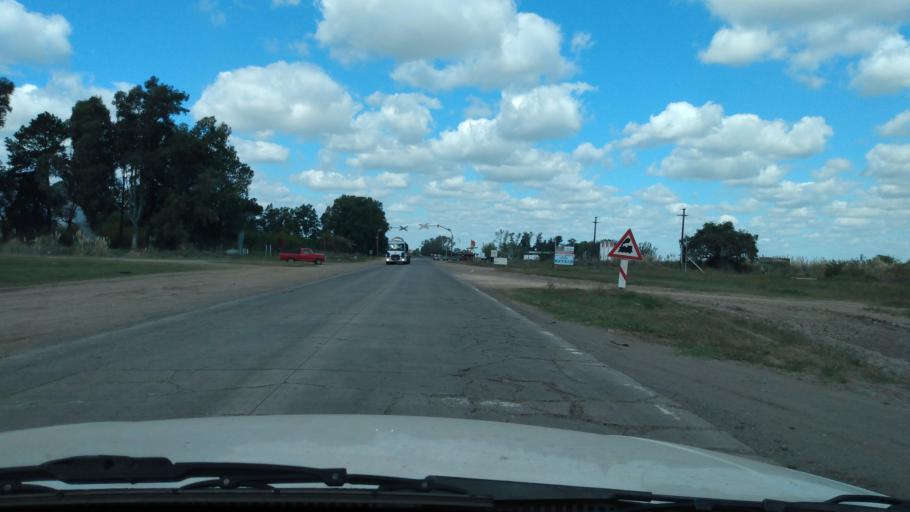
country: AR
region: Buenos Aires
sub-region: Partido de Navarro
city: Navarro
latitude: -34.9953
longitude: -59.3146
